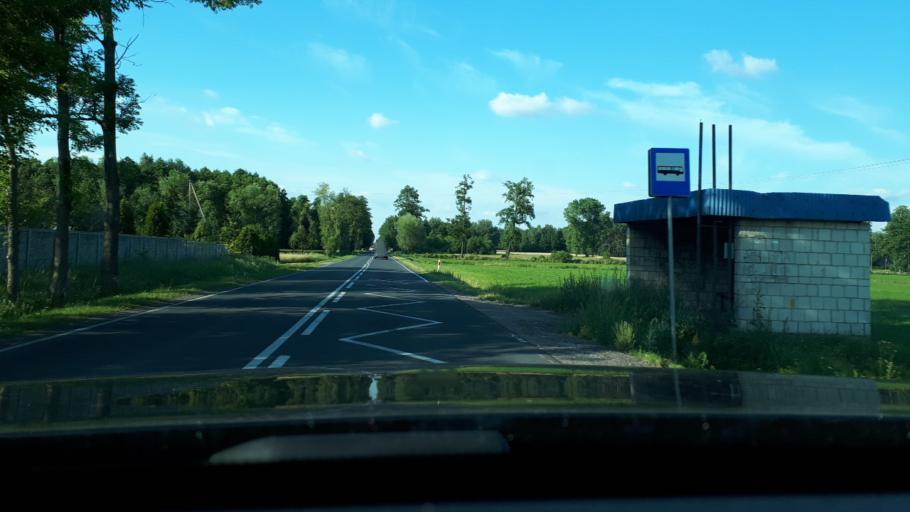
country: PL
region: Masovian Voivodeship
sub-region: Powiat plonski
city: Sochocin
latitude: 52.7069
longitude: 20.4922
